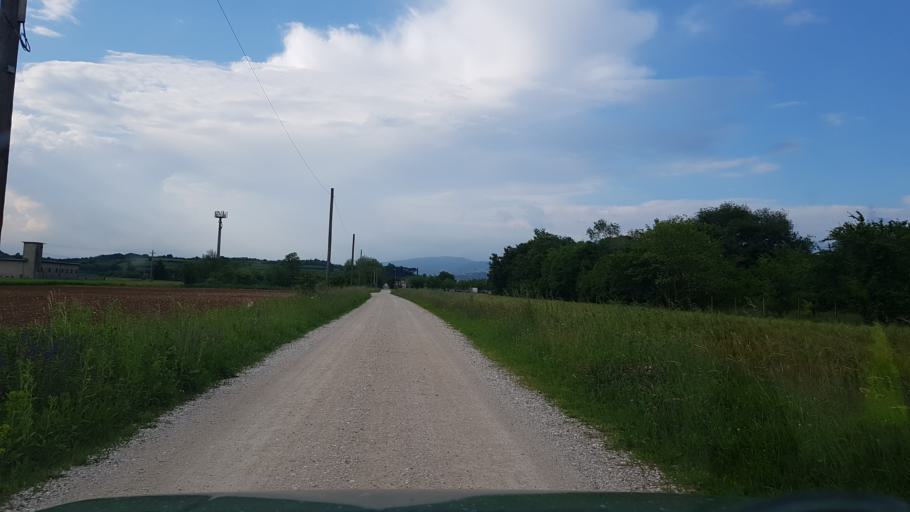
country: IT
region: Friuli Venezia Giulia
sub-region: Provincia di Gorizia
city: Mossa
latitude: 45.9271
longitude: 13.5426
